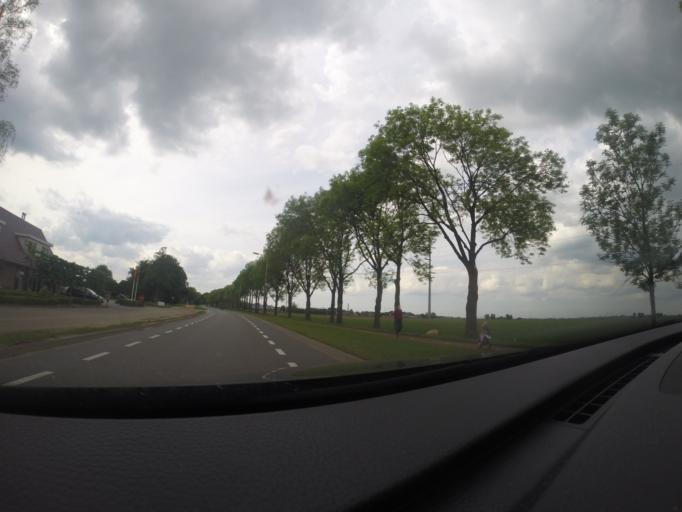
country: NL
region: Gelderland
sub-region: Gemeente Hattem
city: Hattem
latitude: 52.5340
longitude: 6.0236
